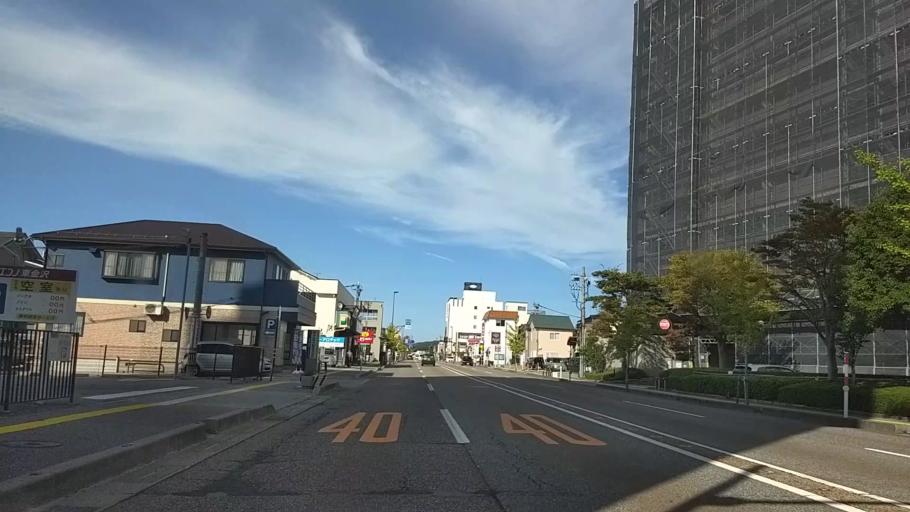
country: JP
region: Ishikawa
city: Kanazawa-shi
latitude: 36.5817
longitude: 136.6715
